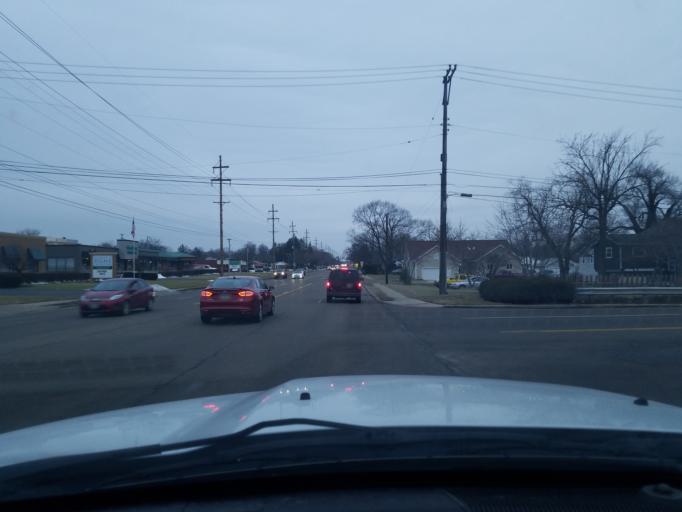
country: US
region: Ohio
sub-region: Montgomery County
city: Kettering
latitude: 39.7040
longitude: -84.1493
